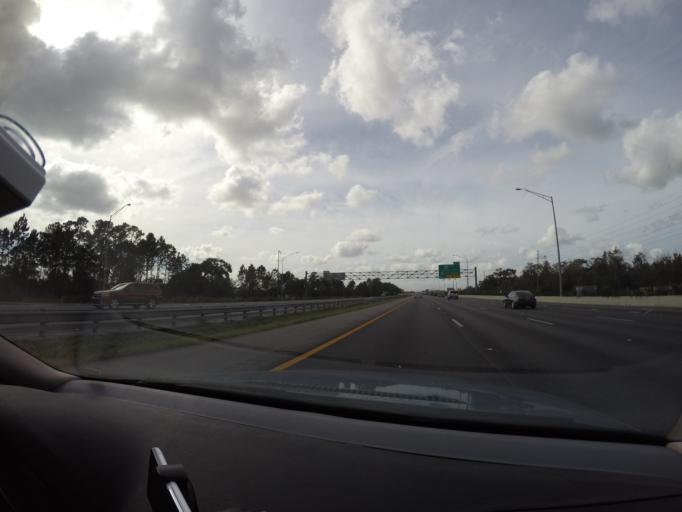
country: US
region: Florida
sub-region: Orange County
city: Conway
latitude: 28.4503
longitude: -81.2928
